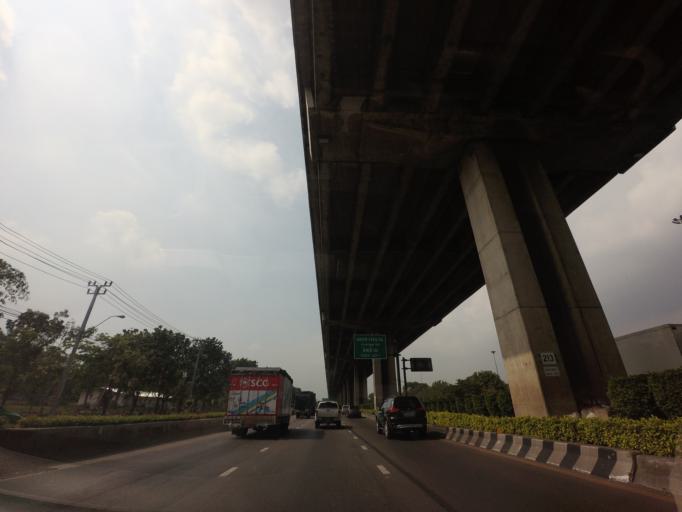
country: TH
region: Bangkok
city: Thawi Watthana
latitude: 13.7844
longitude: 100.3930
